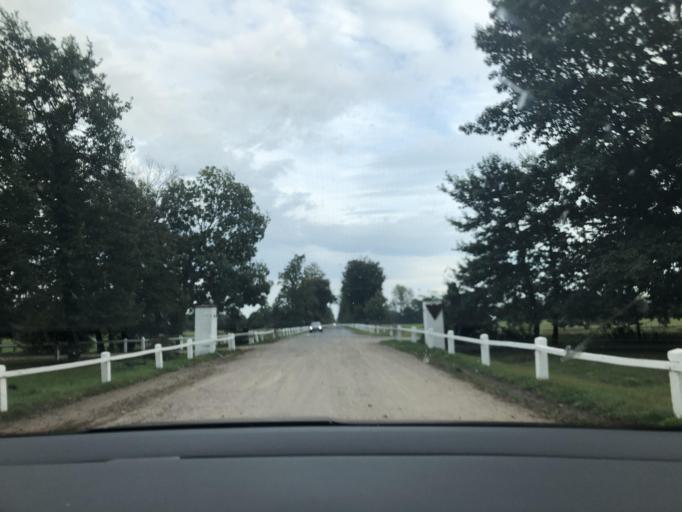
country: CZ
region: Pardubicky
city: Chvaletice
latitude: 50.0531
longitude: 15.4395
